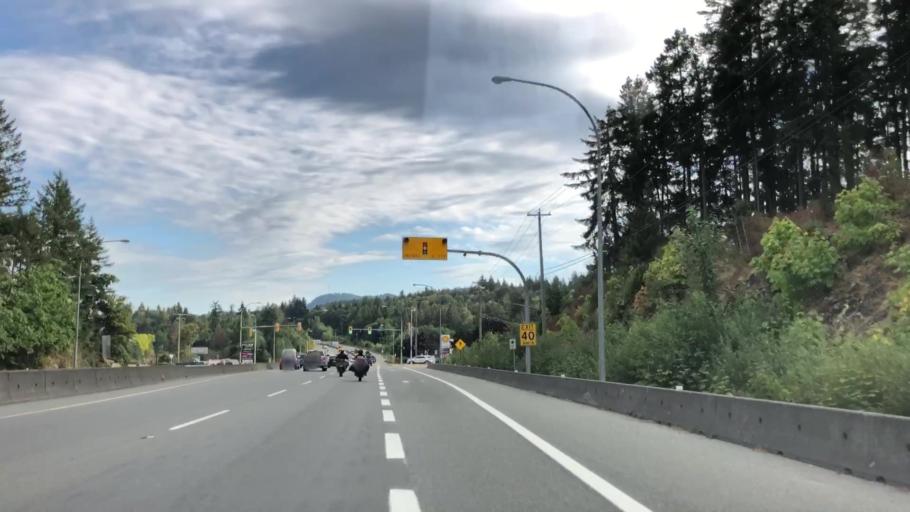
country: CA
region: British Columbia
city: North Saanich
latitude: 48.6539
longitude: -123.5605
